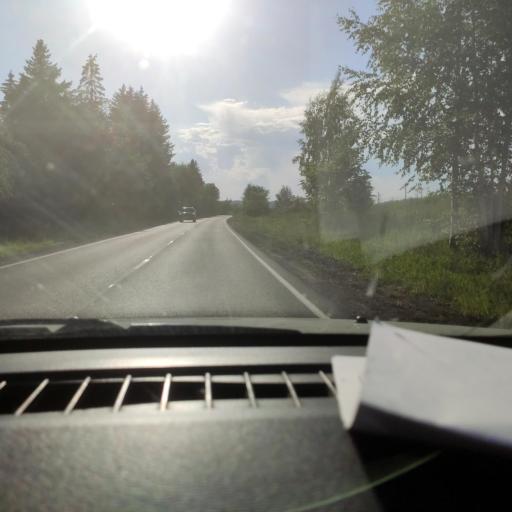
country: RU
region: Perm
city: Krasnokamsk
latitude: 58.1330
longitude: 55.7647
